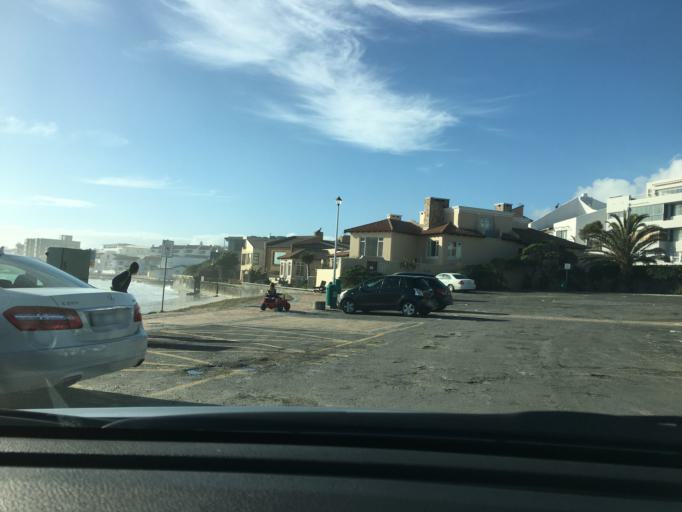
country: ZA
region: Western Cape
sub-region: City of Cape Town
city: Sunset Beach
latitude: -33.7995
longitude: 18.4587
